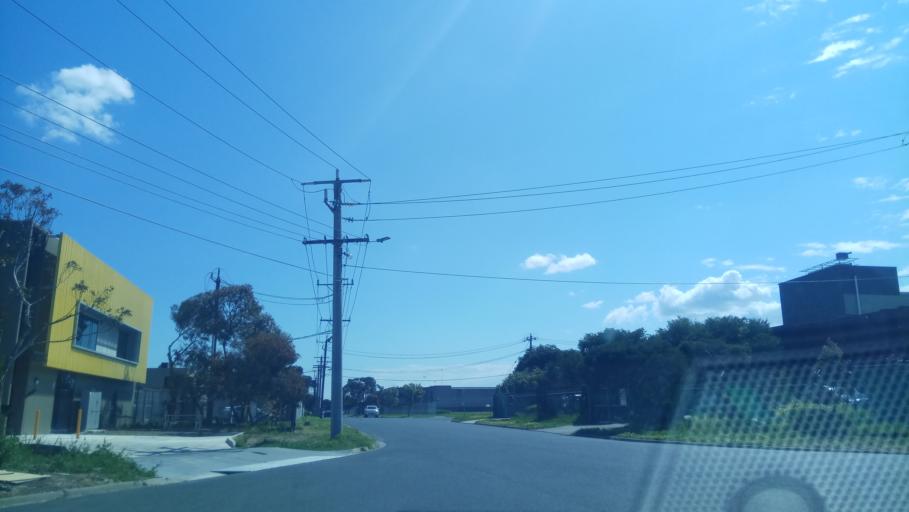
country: AU
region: Victoria
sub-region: Kingston
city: Dingley Village
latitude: -37.9900
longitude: 145.1164
